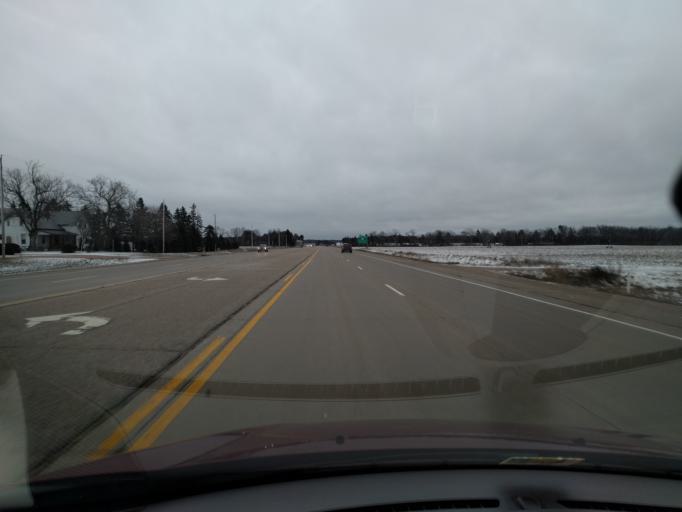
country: US
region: Wisconsin
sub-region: Portage County
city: Whiting
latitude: 44.5227
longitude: -89.4773
